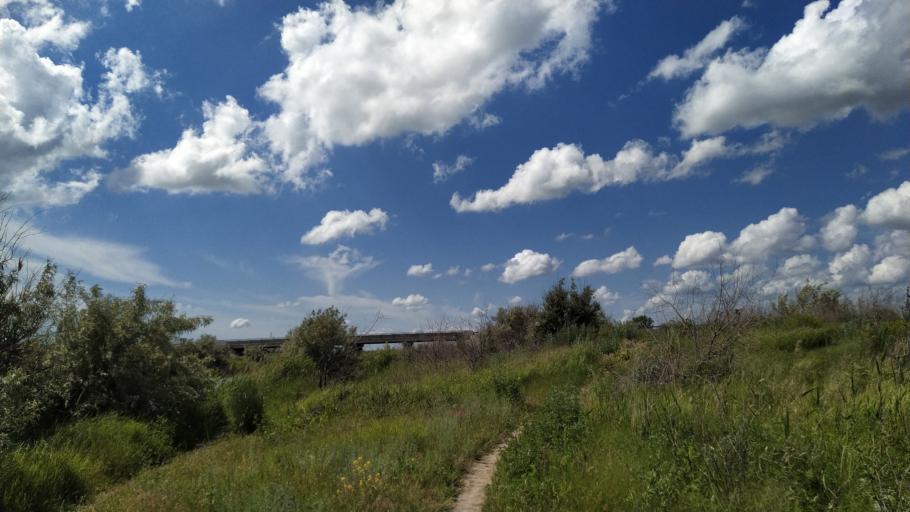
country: RU
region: Rostov
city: Bataysk
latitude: 47.1330
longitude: 39.6785
